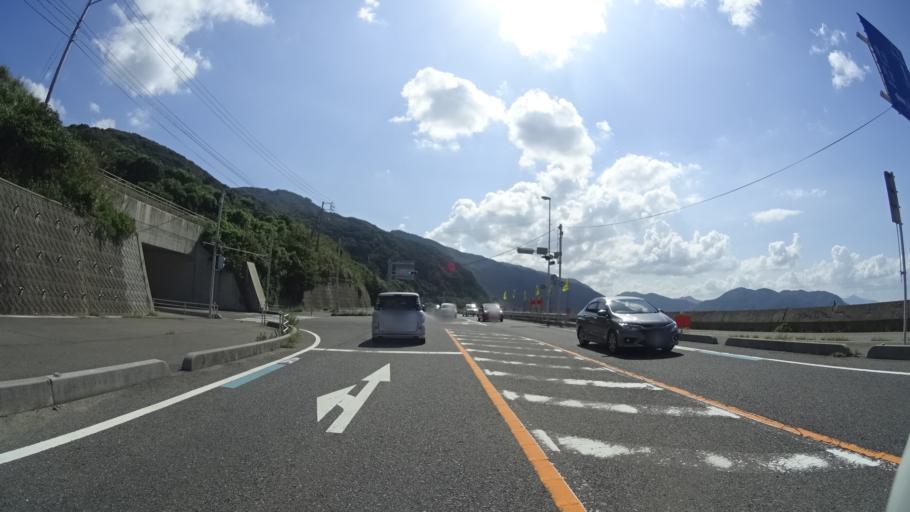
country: JP
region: Yamaguchi
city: Shimonoseki
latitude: 34.2455
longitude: 130.9124
